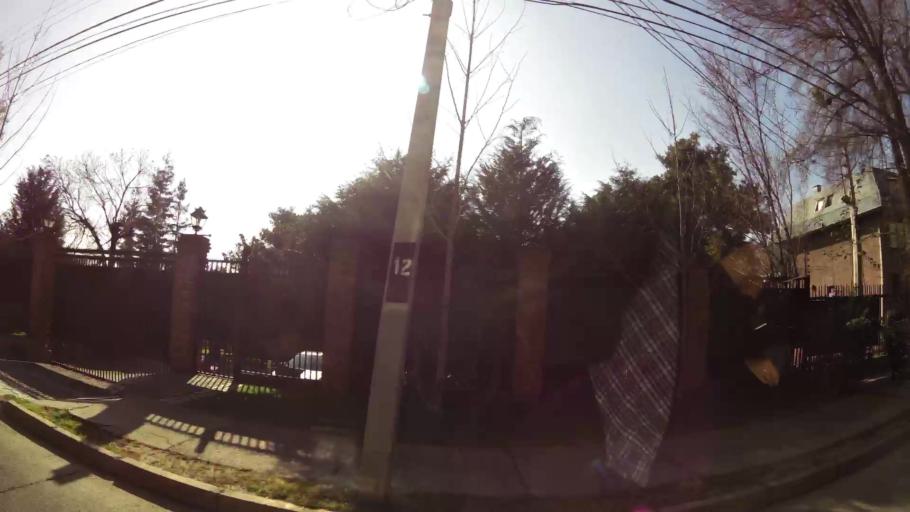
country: CL
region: Santiago Metropolitan
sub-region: Provincia de Santiago
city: Villa Presidente Frei, Nunoa, Santiago, Chile
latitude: -33.3657
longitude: -70.4950
